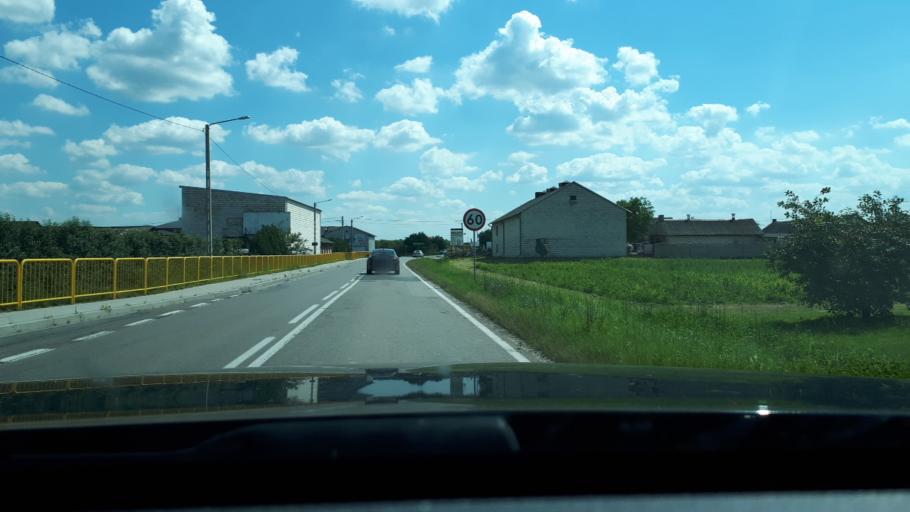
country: PL
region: Masovian Voivodeship
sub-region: Powiat grojecki
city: Warka
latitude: 51.8239
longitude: 21.1938
